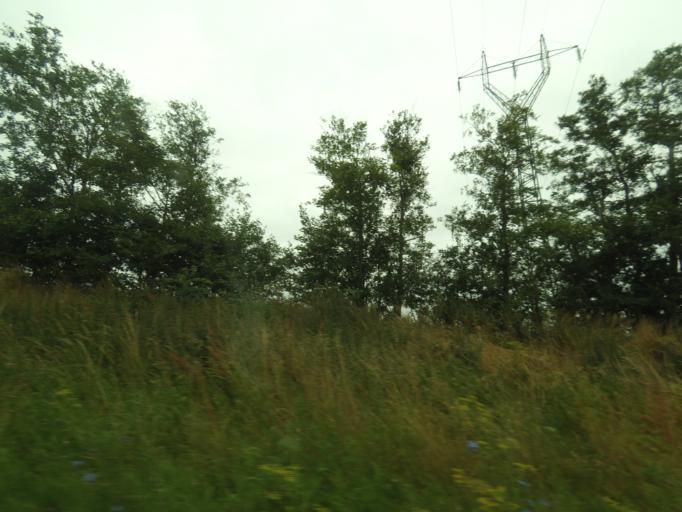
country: DK
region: South Denmark
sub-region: Odense Kommune
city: Stige
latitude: 55.4427
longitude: 10.3764
